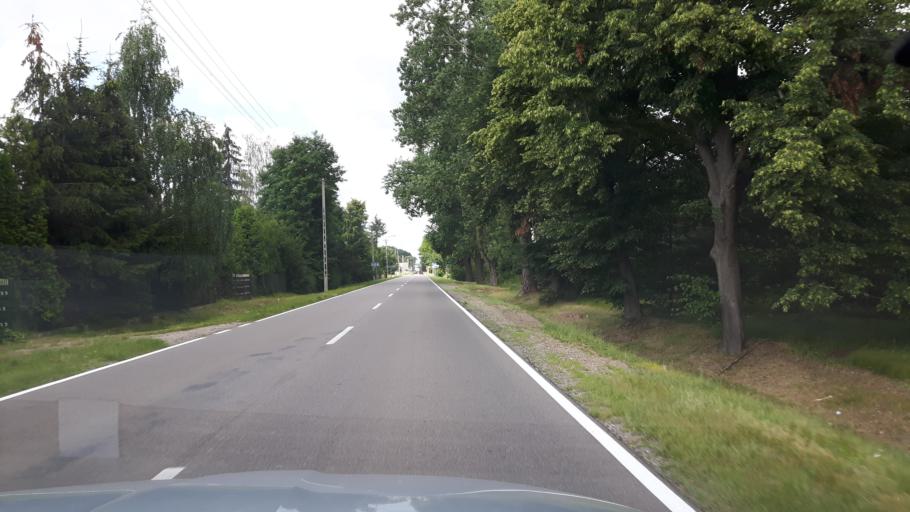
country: PL
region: Masovian Voivodeship
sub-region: Powiat ostrowski
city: Brok
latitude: 52.7039
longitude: 21.8969
